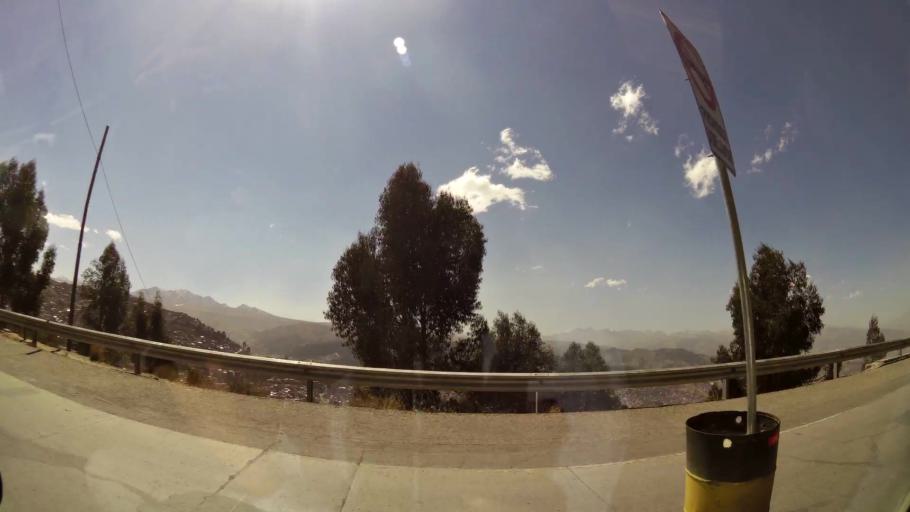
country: BO
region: La Paz
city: La Paz
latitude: -16.4960
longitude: -68.1649
